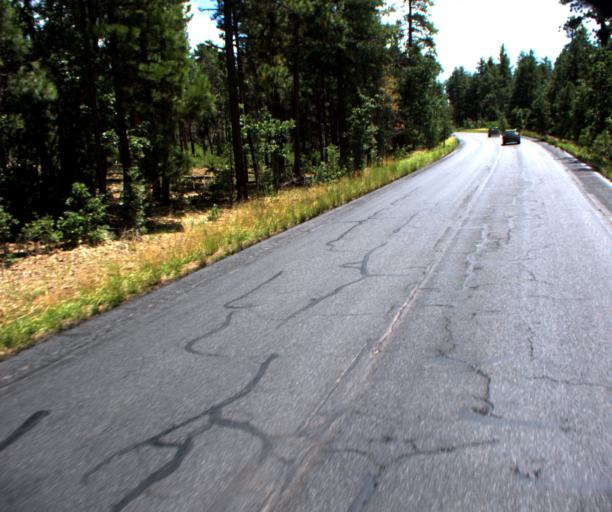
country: US
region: Arizona
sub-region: Gila County
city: Pine
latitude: 34.4682
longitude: -111.4479
